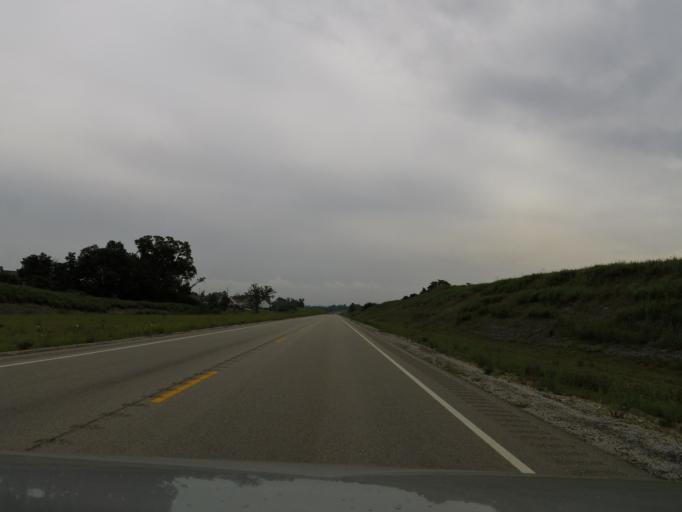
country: US
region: Ohio
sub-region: Brown County
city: Aberdeen
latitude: 38.6095
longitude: -83.8320
